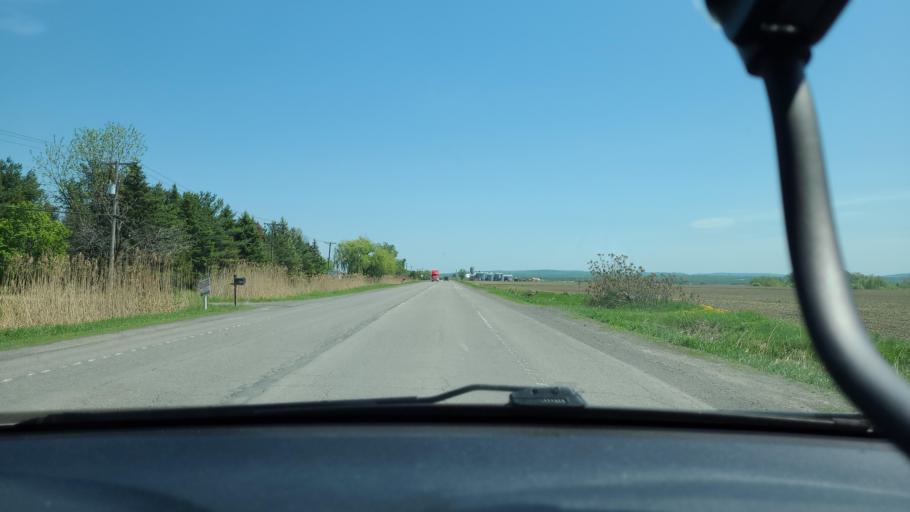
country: CA
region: Quebec
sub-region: Laurentides
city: Mirabel
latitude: 45.6456
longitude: -74.1439
